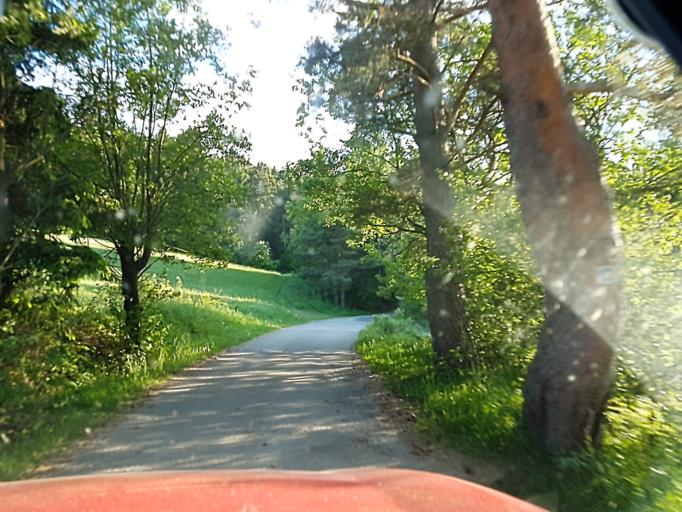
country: SK
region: Zilinsky
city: Ruzomberok
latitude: 49.0729
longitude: 19.2822
